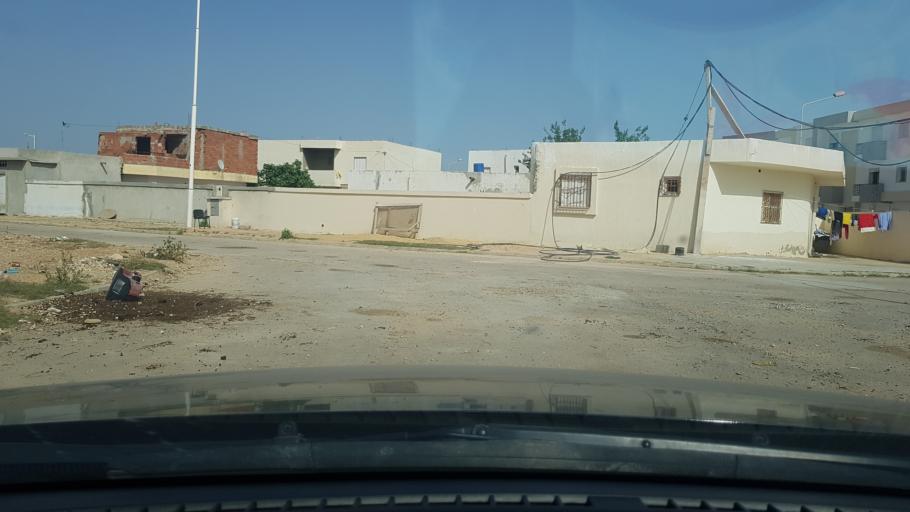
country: TN
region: Safaqis
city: Al Qarmadah
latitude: 34.8316
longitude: 10.7524
